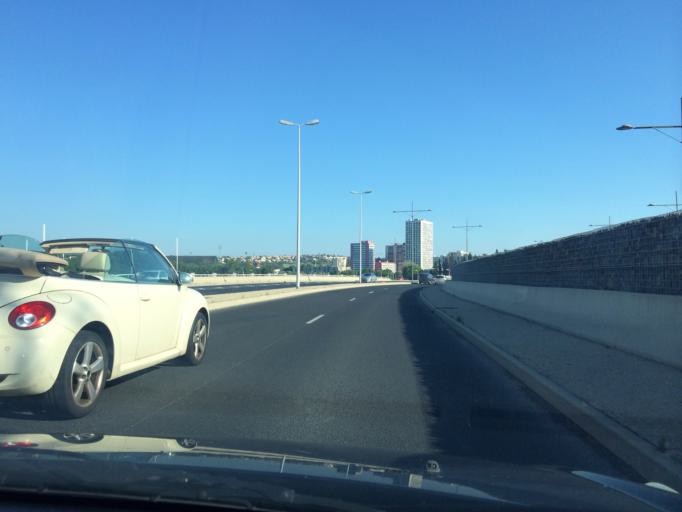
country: FR
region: Languedoc-Roussillon
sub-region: Departement de l'Herault
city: Juvignac
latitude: 43.6158
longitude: 3.8207
